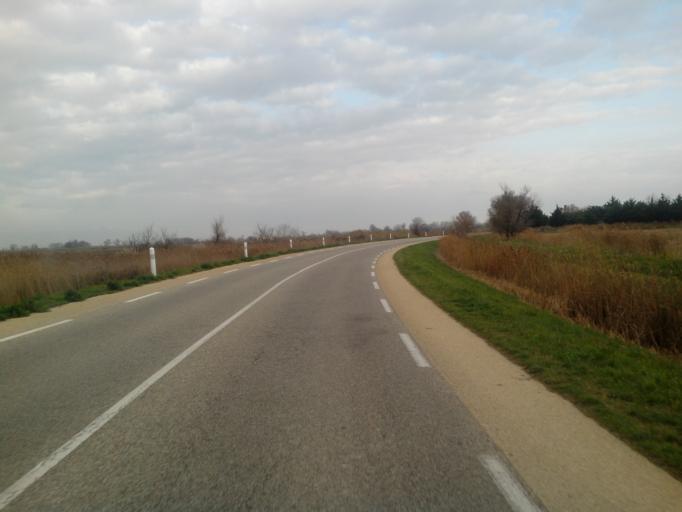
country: FR
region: Languedoc-Roussillon
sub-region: Departement du Gard
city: Saint-Gilles
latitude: 43.5725
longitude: 4.4206
